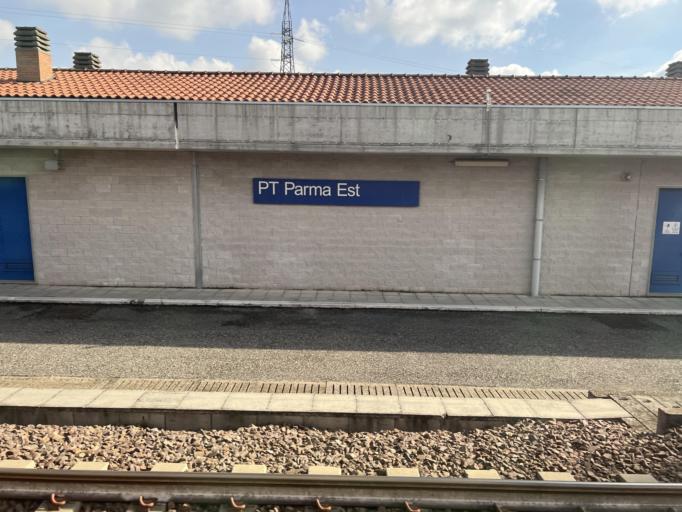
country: IT
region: Emilia-Romagna
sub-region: Provincia di Parma
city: Parma
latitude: 44.8208
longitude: 10.3591
